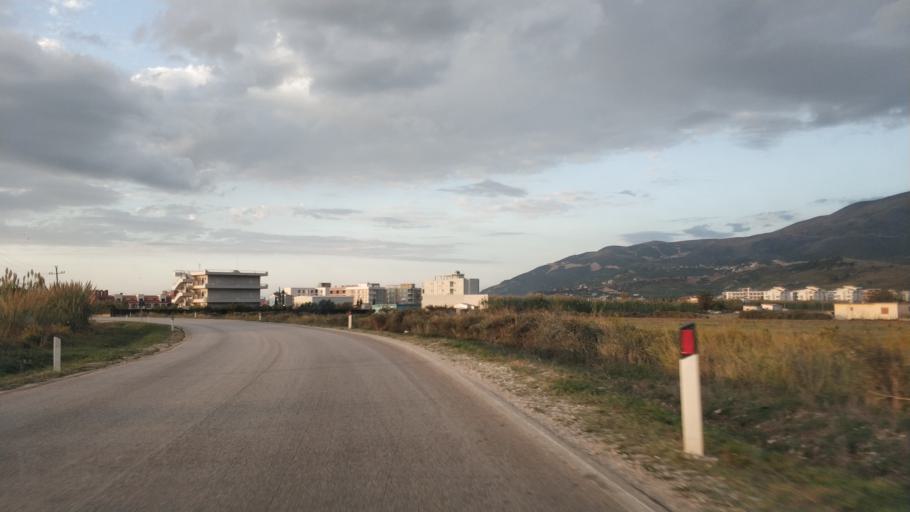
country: AL
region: Vlore
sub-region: Rrethi i Vlores
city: Orikum
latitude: 40.3354
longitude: 19.4767
